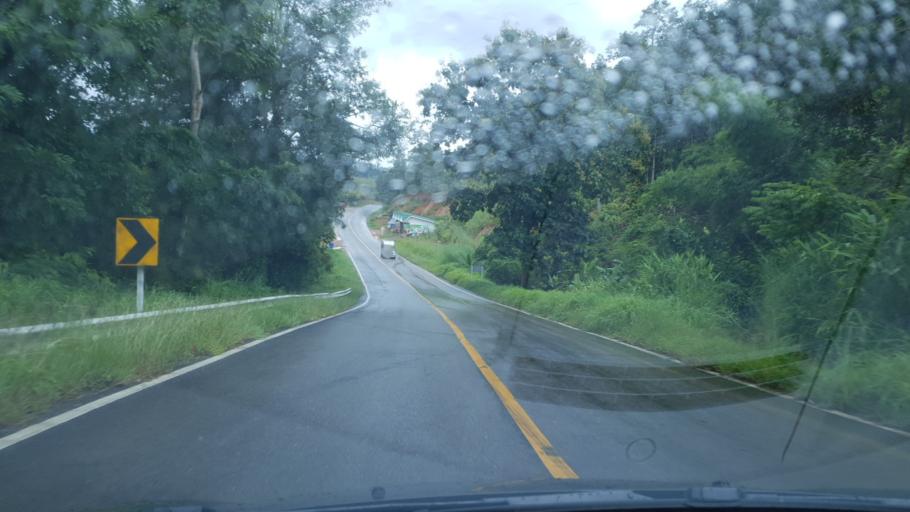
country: TH
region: Mae Hong Son
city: Mae La Noi
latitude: 18.5423
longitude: 97.9383
